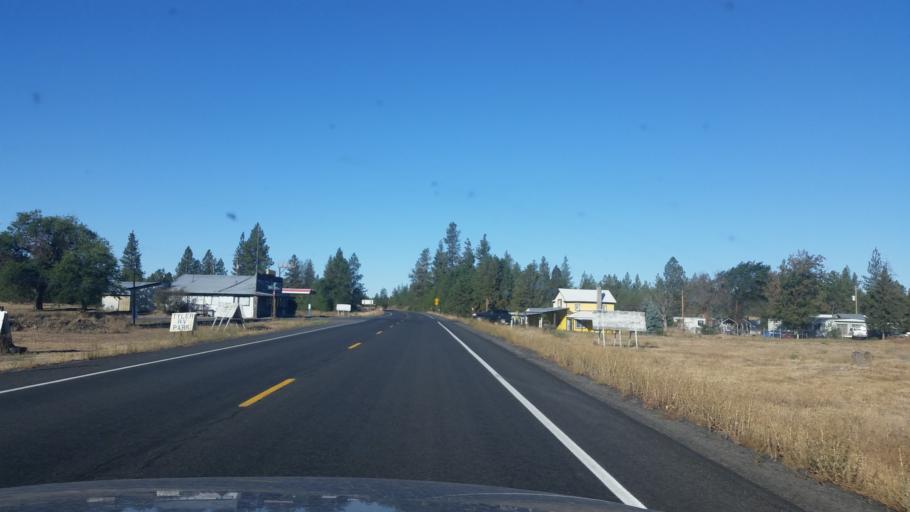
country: US
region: Washington
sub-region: Spokane County
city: Medical Lake
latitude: 47.4360
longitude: -117.7820
